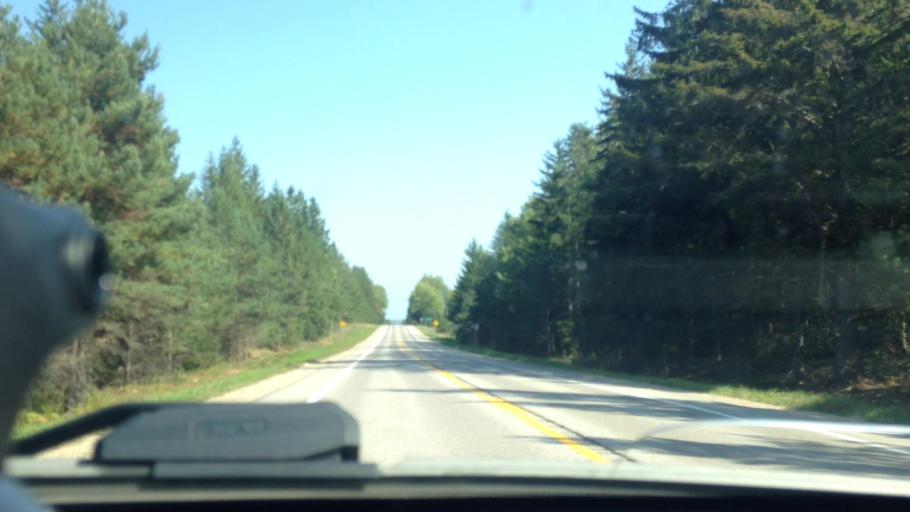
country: US
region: Michigan
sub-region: Luce County
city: Newberry
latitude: 46.3037
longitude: -85.4436
